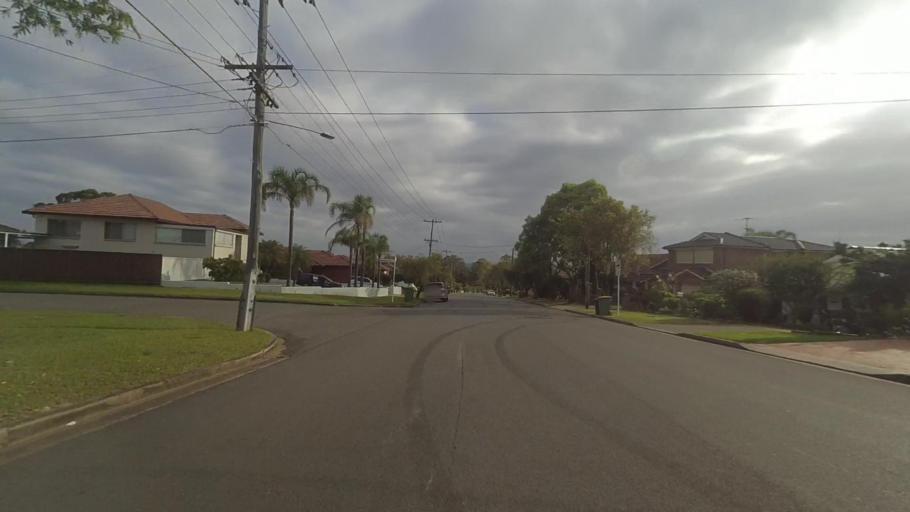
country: AU
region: New South Wales
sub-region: Bankstown
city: Milperra
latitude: -33.9125
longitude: 151.0001
